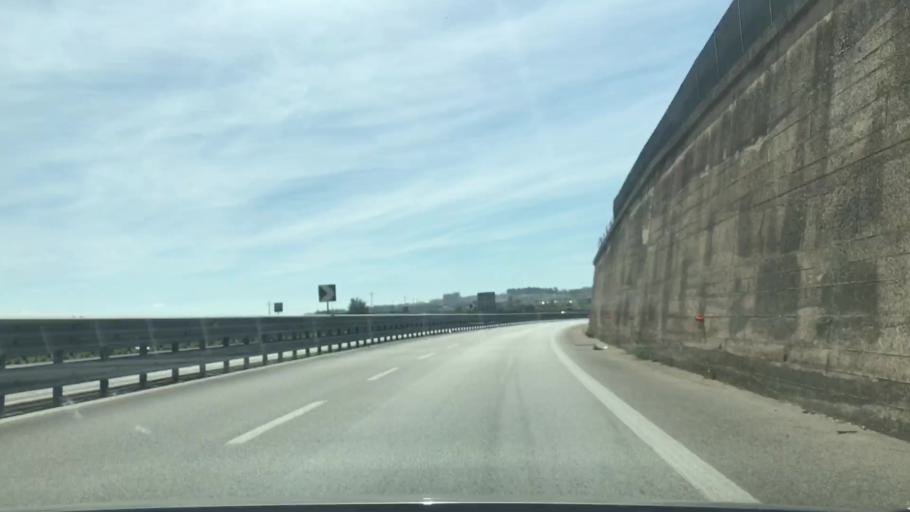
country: IT
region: Basilicate
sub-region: Provincia di Matera
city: Matera
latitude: 40.6943
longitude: 16.5907
